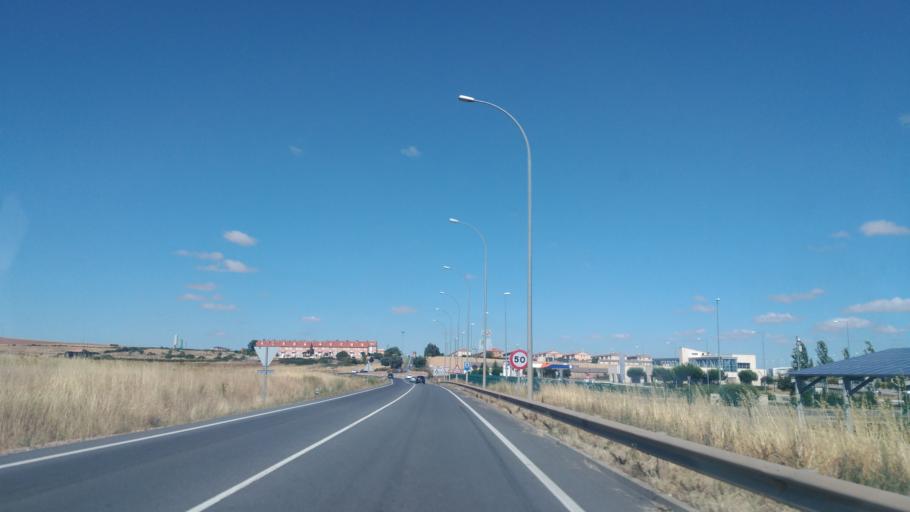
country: ES
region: Castille and Leon
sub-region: Provincia de Salamanca
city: Doninos de Salamanca
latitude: 40.9590
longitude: -5.7252
